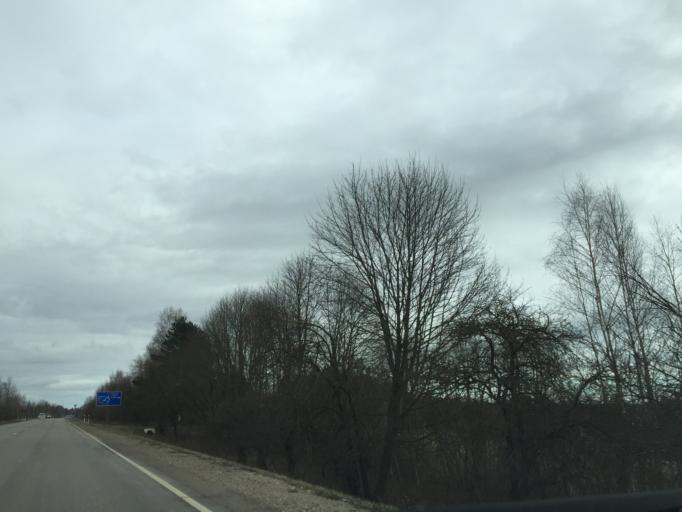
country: LV
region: Daugavpils
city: Daugavpils
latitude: 55.9156
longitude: 26.6660
